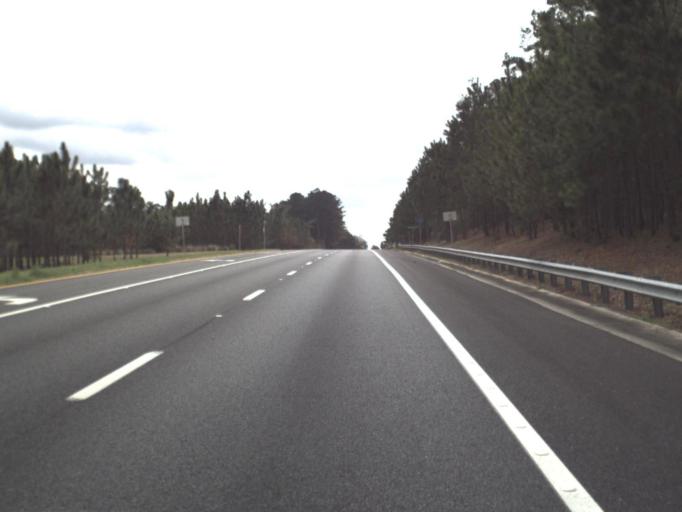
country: US
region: Georgia
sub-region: Grady County
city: Cairo
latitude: 30.6725
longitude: -84.1602
